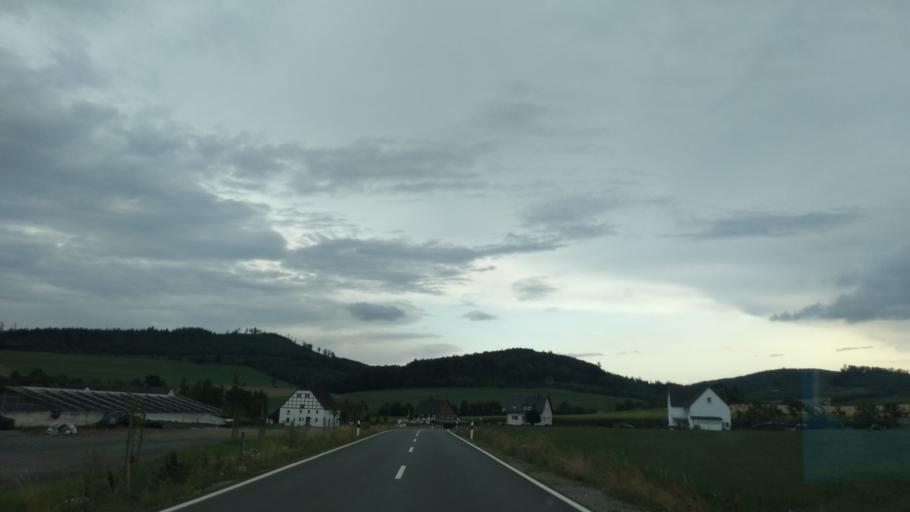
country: DE
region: North Rhine-Westphalia
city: Balve
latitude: 51.3040
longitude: 7.9306
